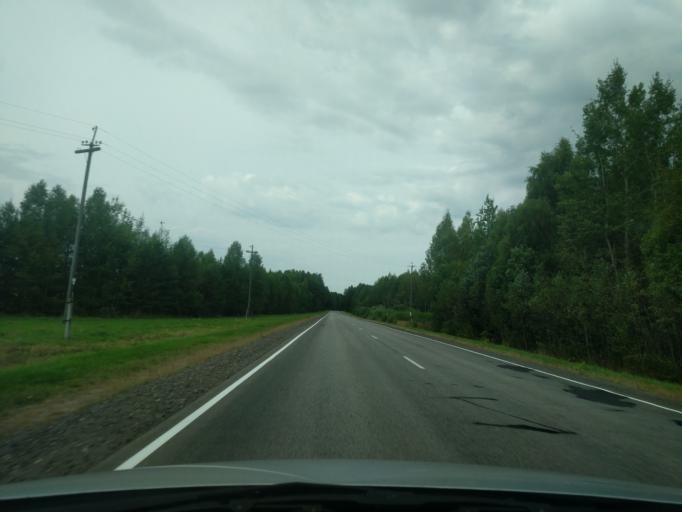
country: RU
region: Kirov
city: Svecha
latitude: 58.2718
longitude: 47.7333
